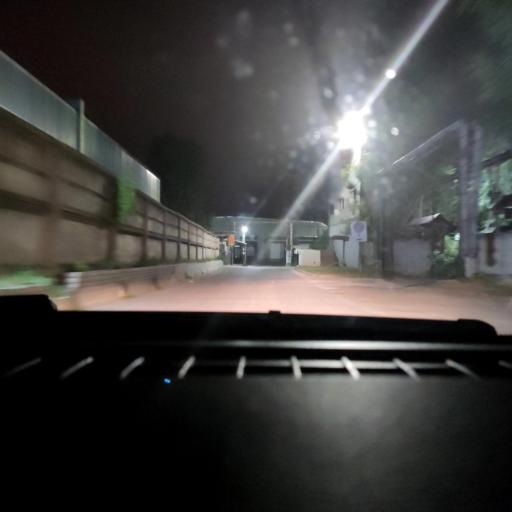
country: RU
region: Voronezj
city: Somovo
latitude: 51.7211
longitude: 39.2859
